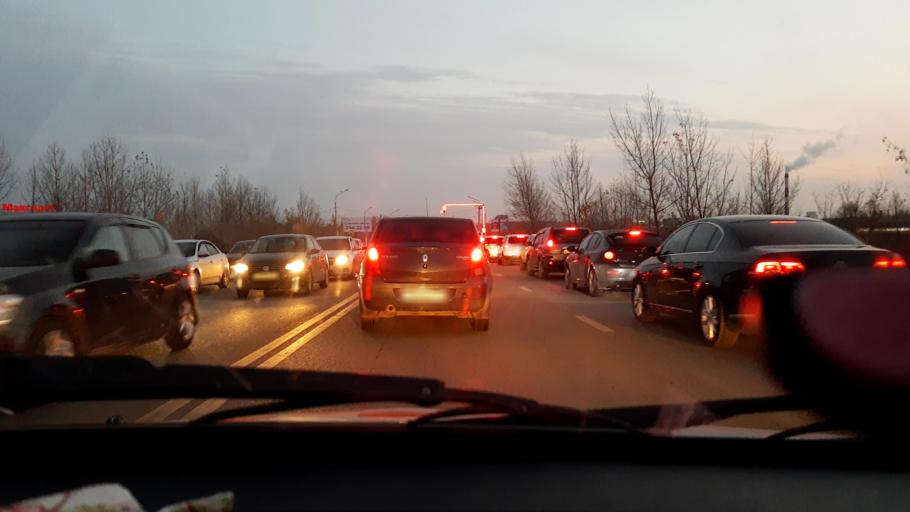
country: RU
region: Bashkortostan
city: Ufa
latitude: 54.7938
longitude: 56.0771
